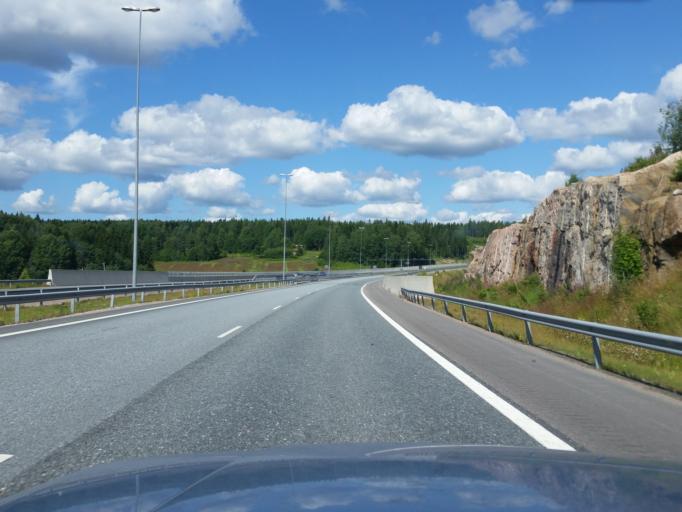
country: FI
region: Uusimaa
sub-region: Helsinki
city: Saukkola
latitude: 60.3288
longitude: 23.9357
